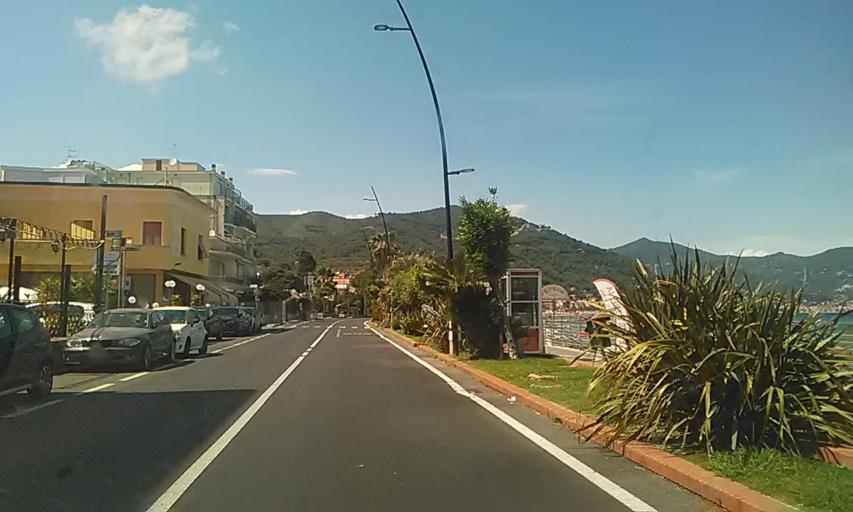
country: IT
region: Liguria
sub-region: Provincia di Savona
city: Laigueglia
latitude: 43.9715
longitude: 8.1604
